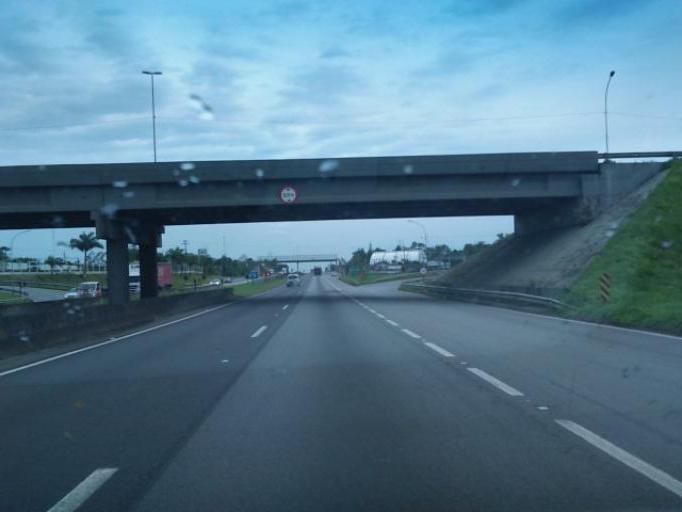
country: BR
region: Sao Paulo
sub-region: Registro
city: Registro
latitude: -24.4578
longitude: -47.8148
